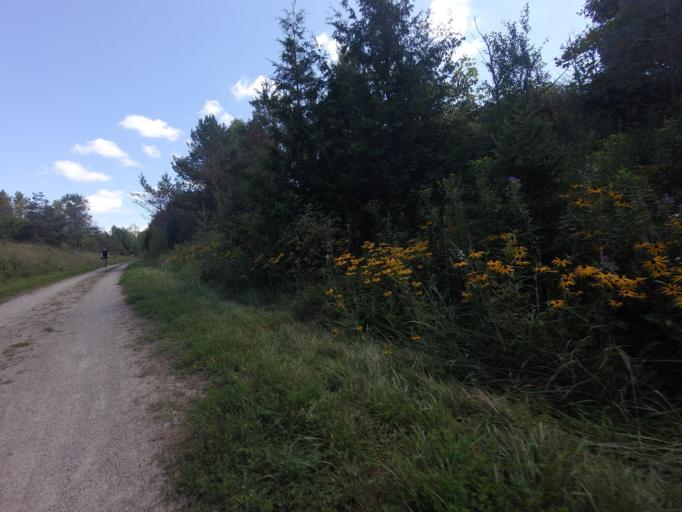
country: CA
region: Ontario
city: Orangeville
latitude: 43.7935
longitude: -80.3111
